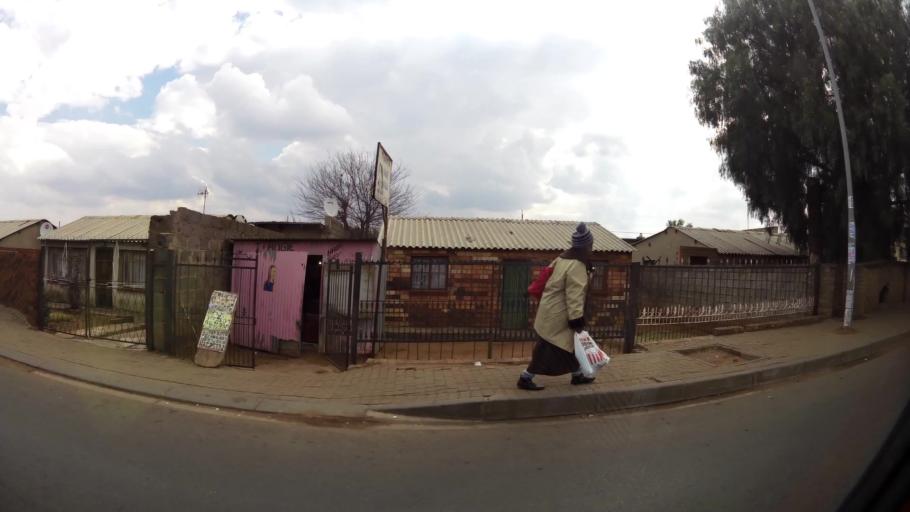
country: ZA
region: Gauteng
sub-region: City of Johannesburg Metropolitan Municipality
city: Soweto
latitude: -26.2469
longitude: 27.8542
